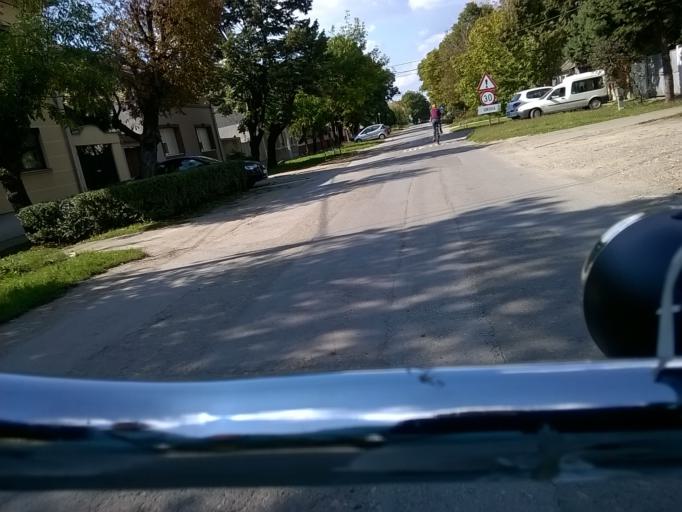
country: RS
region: Autonomna Pokrajina Vojvodina
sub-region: Juznobanatski Okrug
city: Pancevo
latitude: 44.8775
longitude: 20.6366
